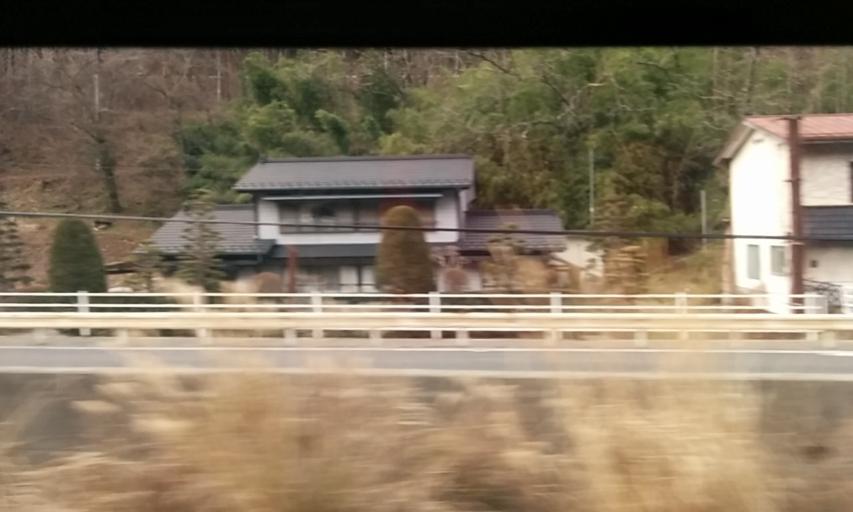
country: JP
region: Nagano
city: Shiojiri
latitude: 36.0196
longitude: 137.8650
